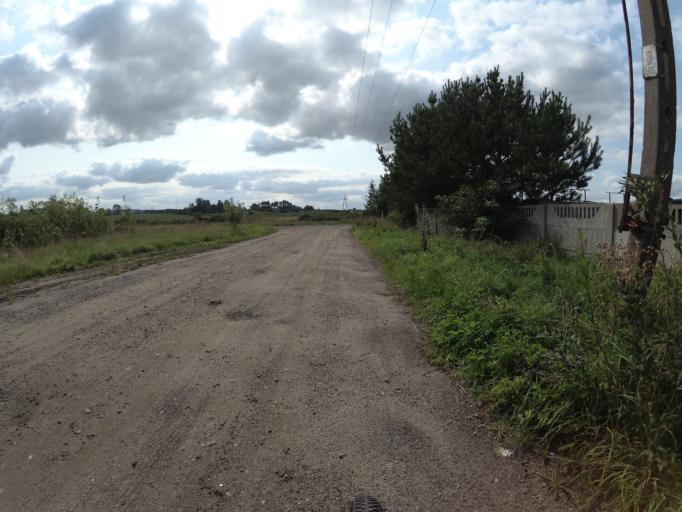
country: PL
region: Pomeranian Voivodeship
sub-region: Powiat wejherowski
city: Bojano
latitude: 54.4993
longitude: 18.4279
